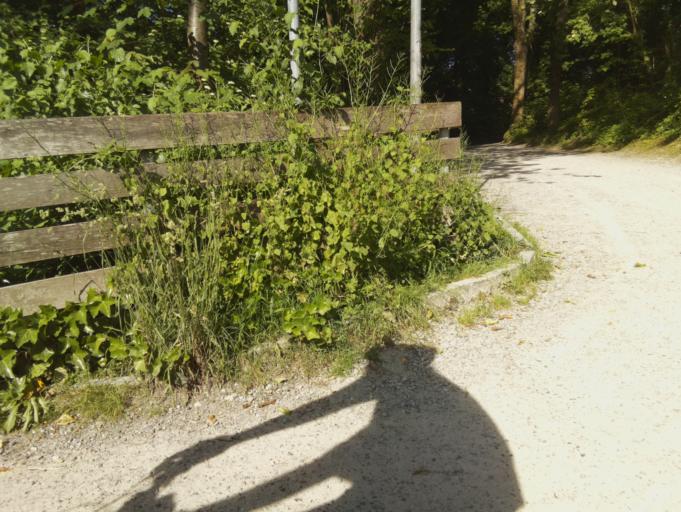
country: CH
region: Zurich
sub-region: Bezirk Meilen
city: Dorf
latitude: 47.2399
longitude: 8.7363
